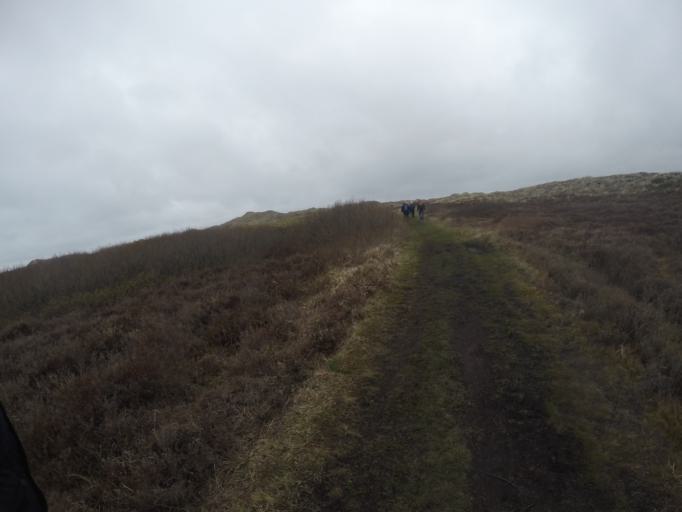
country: DK
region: Central Jutland
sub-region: Lemvig Kommune
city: Thyboron
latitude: 56.8380
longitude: 8.2743
